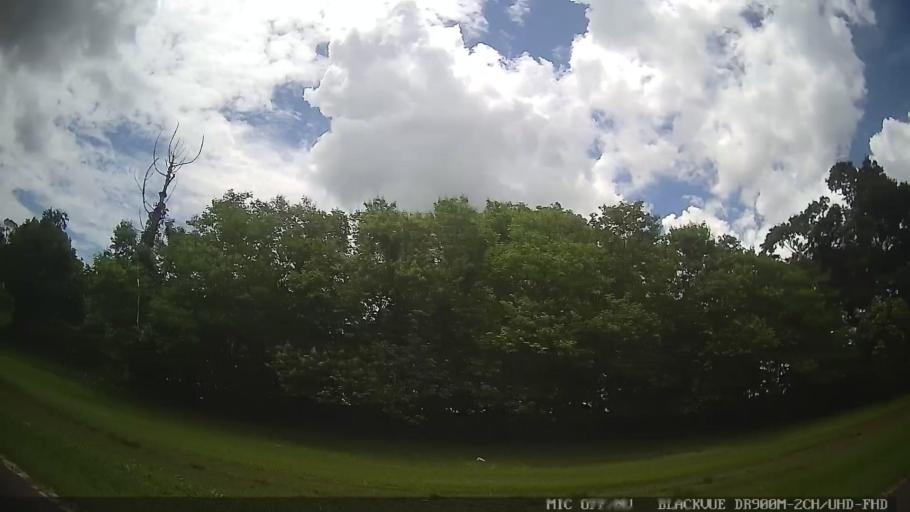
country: BR
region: Sao Paulo
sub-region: Laranjal Paulista
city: Laranjal Paulista
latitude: -23.0402
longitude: -47.9015
